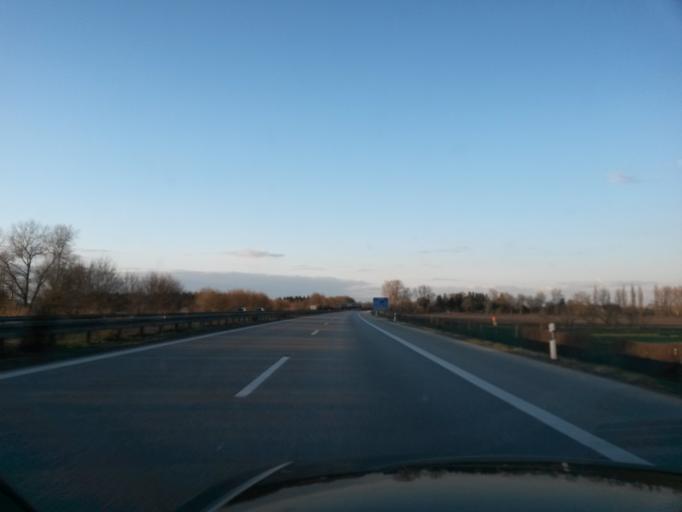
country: DE
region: Bavaria
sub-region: Upper Bavaria
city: Oberschleissheim
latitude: 48.2590
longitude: 11.5346
